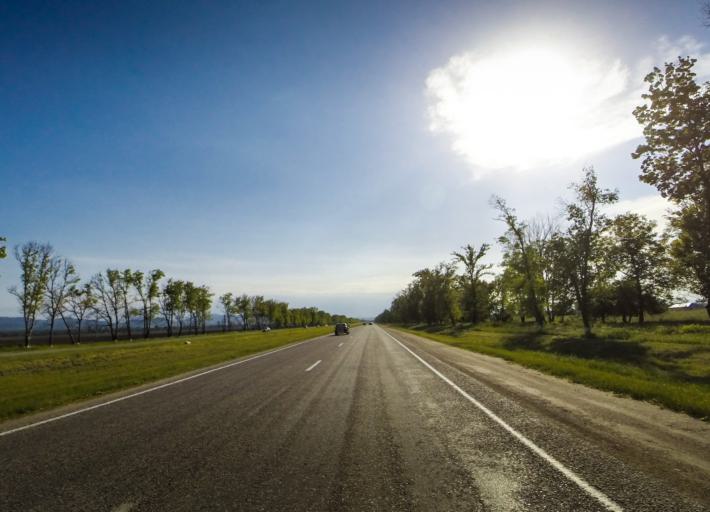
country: RU
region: Kabardino-Balkariya
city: Nartan
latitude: 43.4999
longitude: 43.7123
